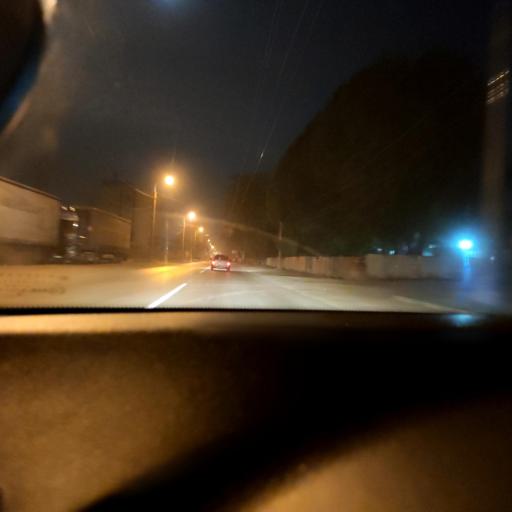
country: RU
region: Samara
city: Samara
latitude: 53.1998
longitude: 50.2670
